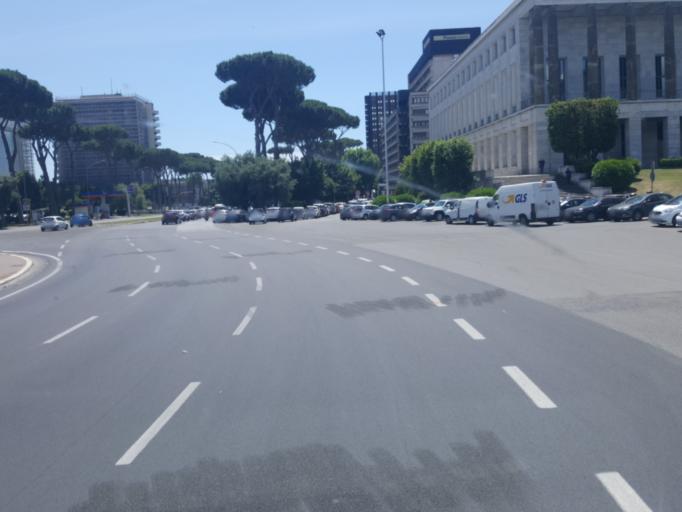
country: IT
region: Latium
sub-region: Citta metropolitana di Roma Capitale
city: Selcetta
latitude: 41.8338
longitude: 12.4705
